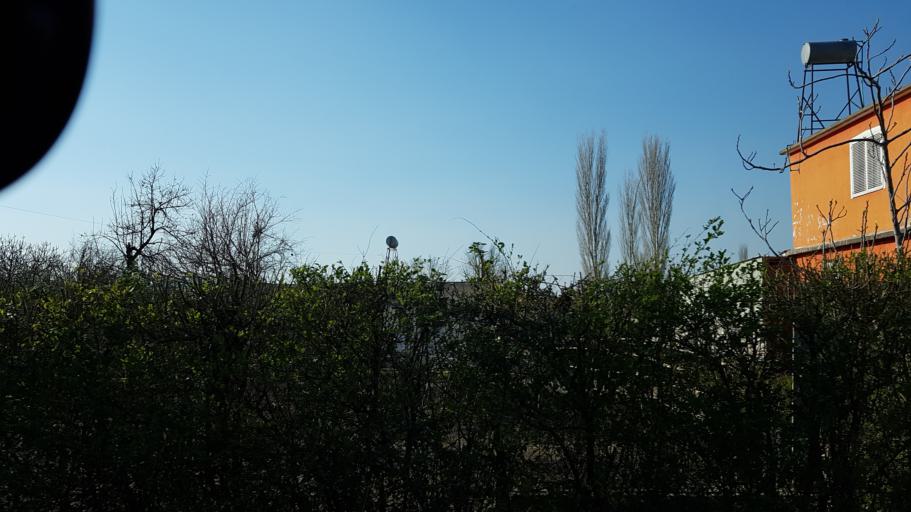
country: AL
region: Shkoder
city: Vukatane
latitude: 41.9930
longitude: 19.5594
